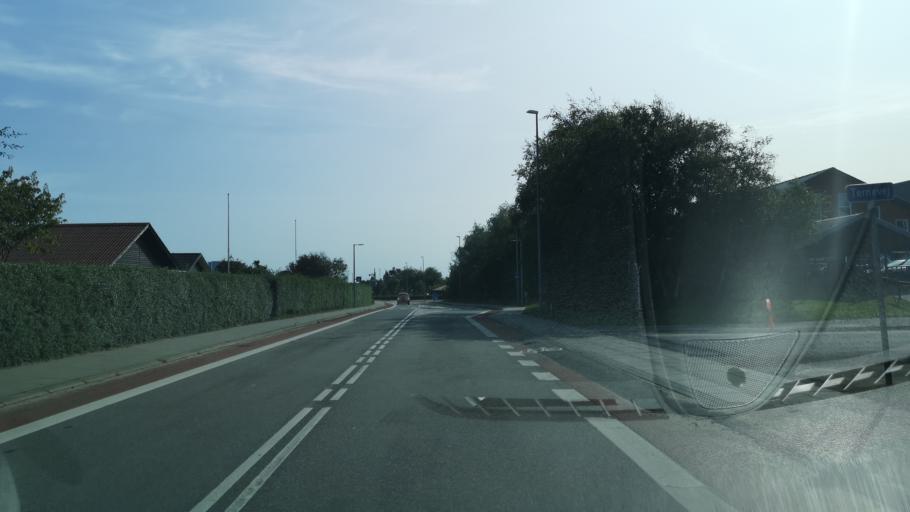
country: DK
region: Central Jutland
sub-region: Ringkobing-Skjern Kommune
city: Videbaek
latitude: 56.0870
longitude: 8.6193
